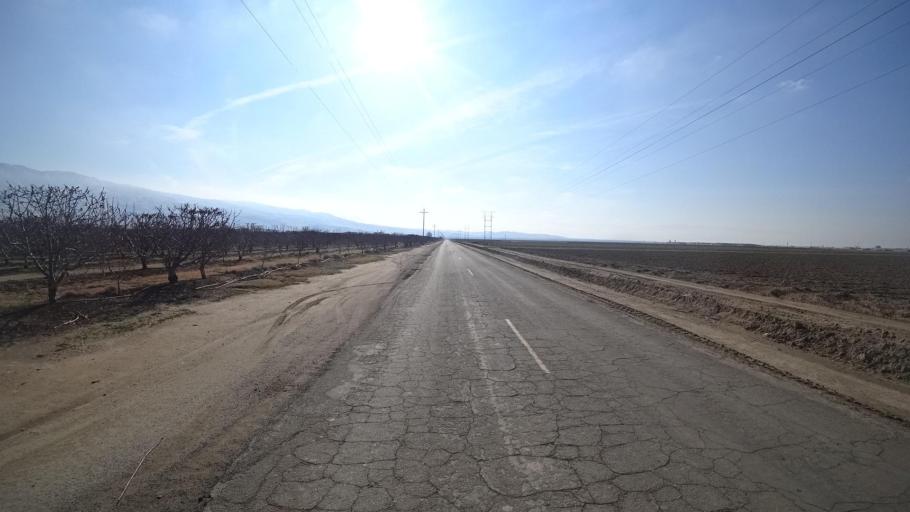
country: US
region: California
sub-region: Kern County
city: Arvin
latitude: 35.2072
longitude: -118.8062
